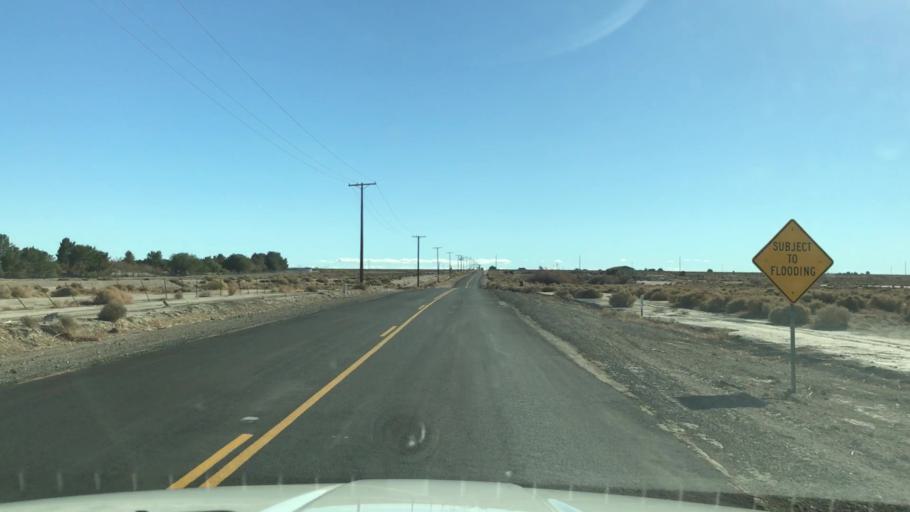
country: US
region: California
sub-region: Kern County
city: California City
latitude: 35.2739
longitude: -117.9857
